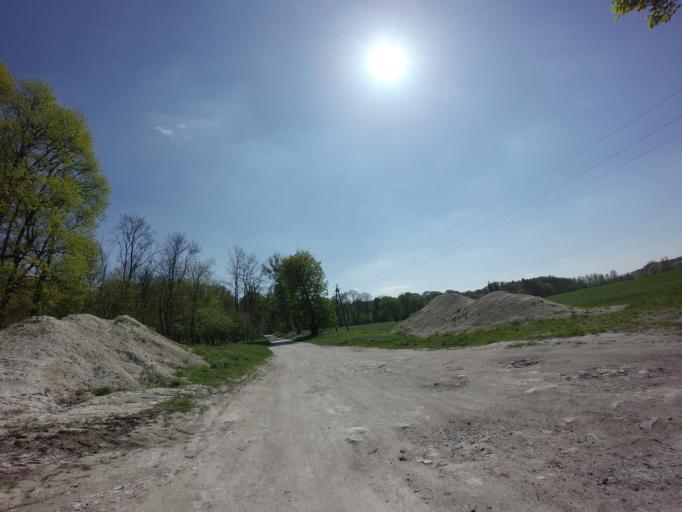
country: PL
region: West Pomeranian Voivodeship
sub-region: Powiat stargardzki
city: Suchan
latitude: 53.1829
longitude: 15.3209
